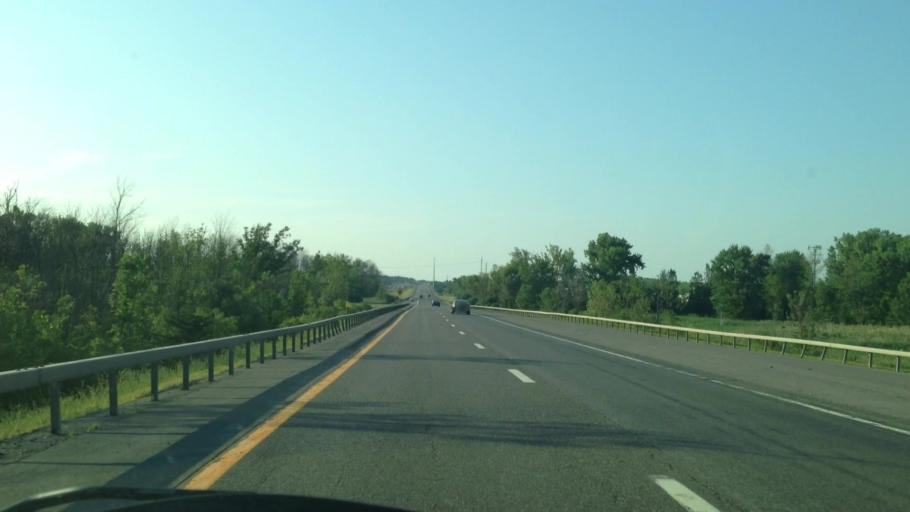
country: US
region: New York
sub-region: Onondaga County
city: East Syracuse
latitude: 43.0544
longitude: -76.0504
